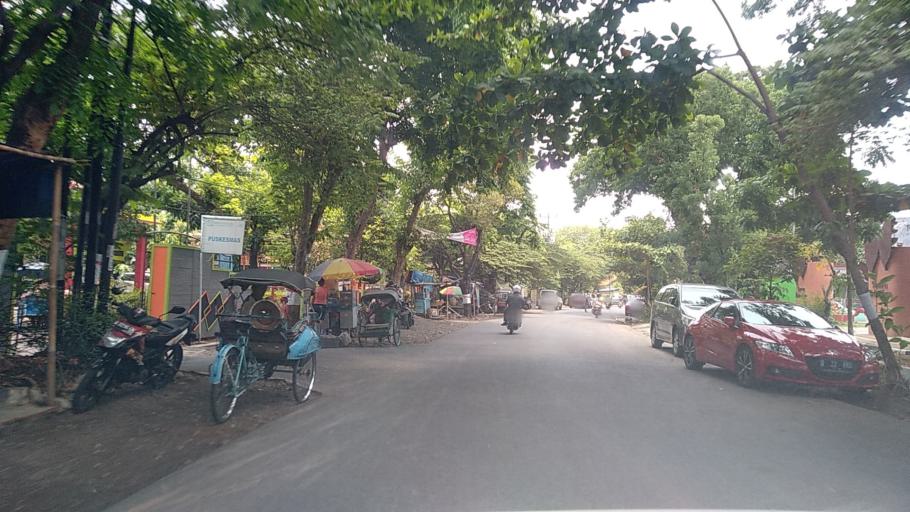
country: ID
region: Central Java
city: Semarang
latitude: -6.9947
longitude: 110.4373
